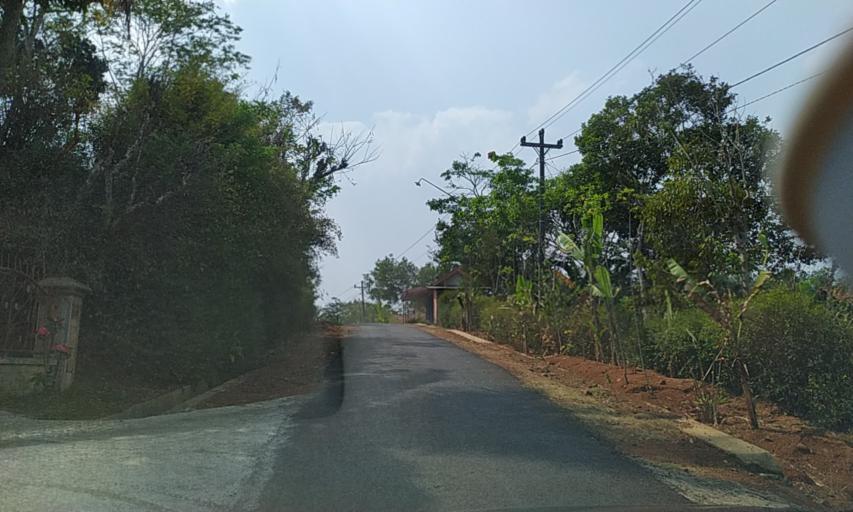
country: ID
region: Central Java
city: Rungkang
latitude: -7.4376
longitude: 108.8532
